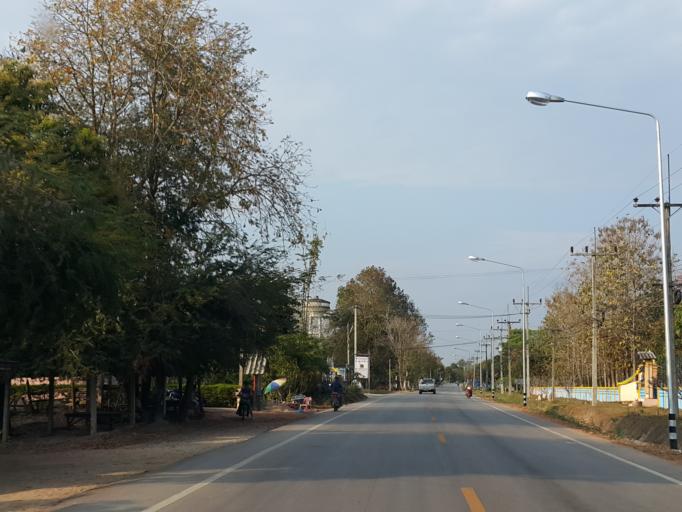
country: TH
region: Lampang
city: Chae Hom
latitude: 18.5337
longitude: 99.4782
